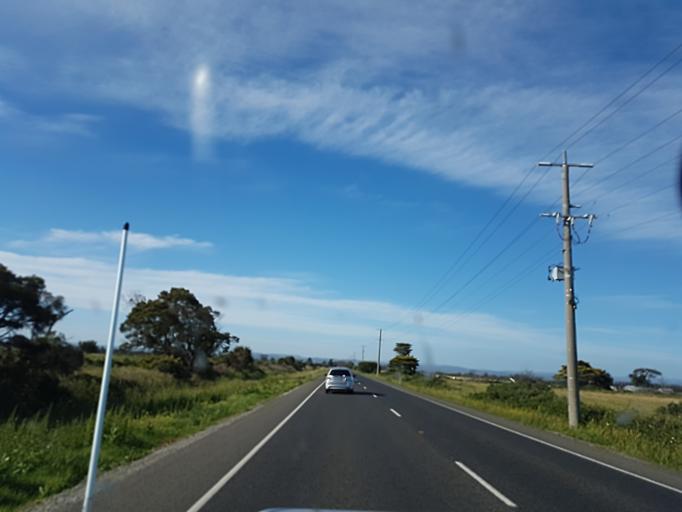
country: AU
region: Victoria
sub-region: Cardinia
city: Pakenham South
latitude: -38.1485
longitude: 145.4867
